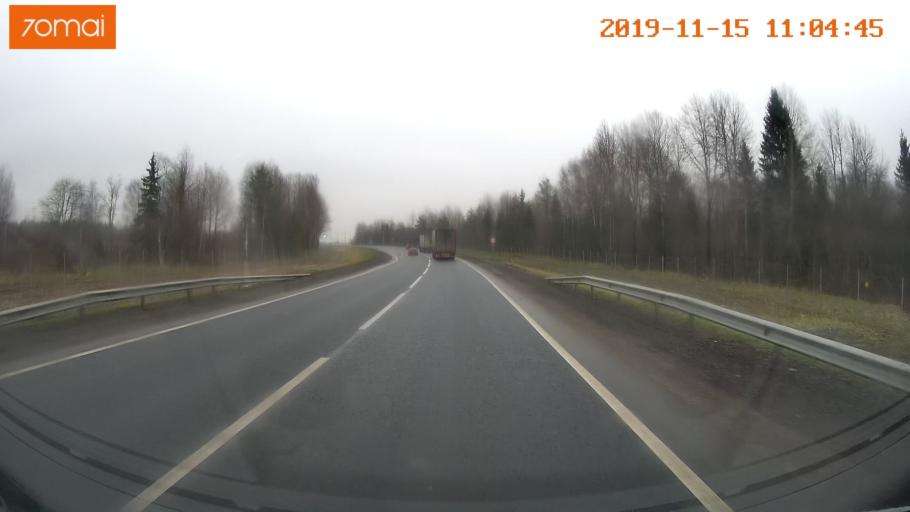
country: RU
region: Vologda
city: Chebsara
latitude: 59.1188
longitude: 38.9899
